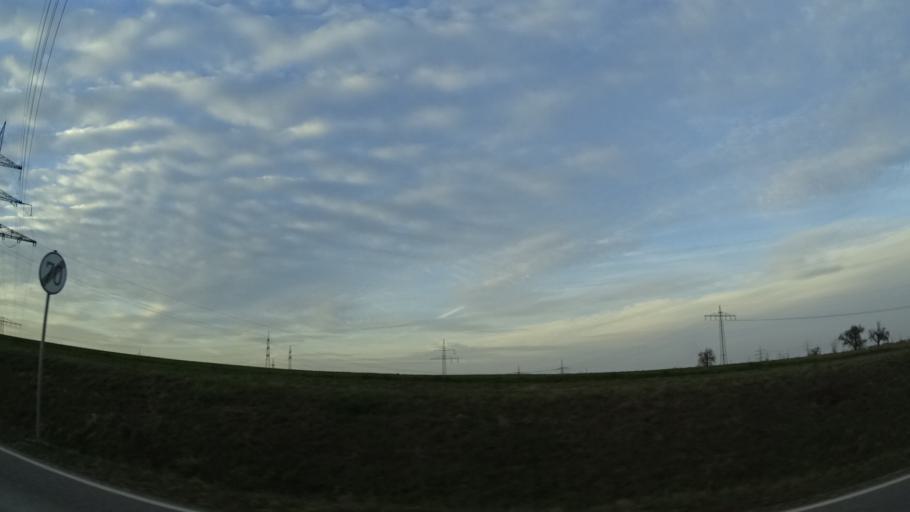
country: DE
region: Baden-Wuerttemberg
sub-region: Regierungsbezirk Stuttgart
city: Markgroningen
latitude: 48.9012
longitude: 9.0566
